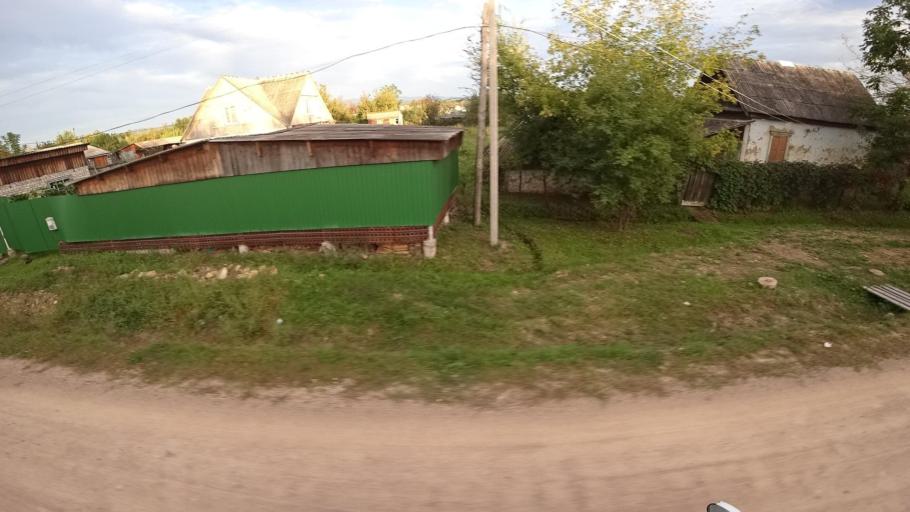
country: RU
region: Primorskiy
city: Yakovlevka
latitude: 44.4260
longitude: 133.4816
